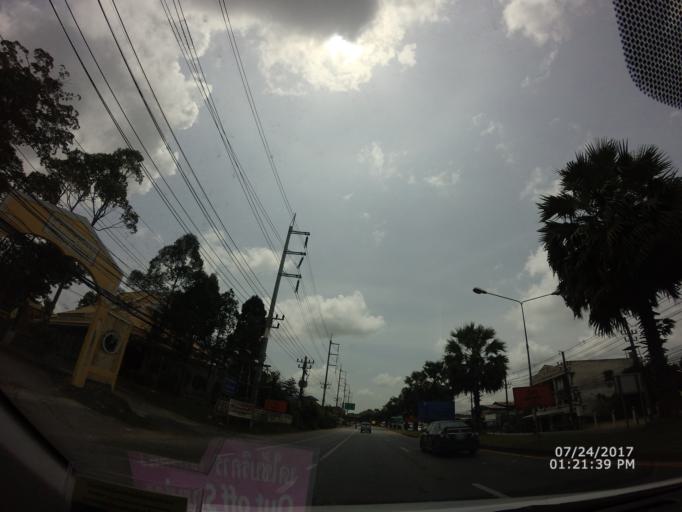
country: TH
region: Phuket
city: Thalang
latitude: 8.0864
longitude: 98.3421
